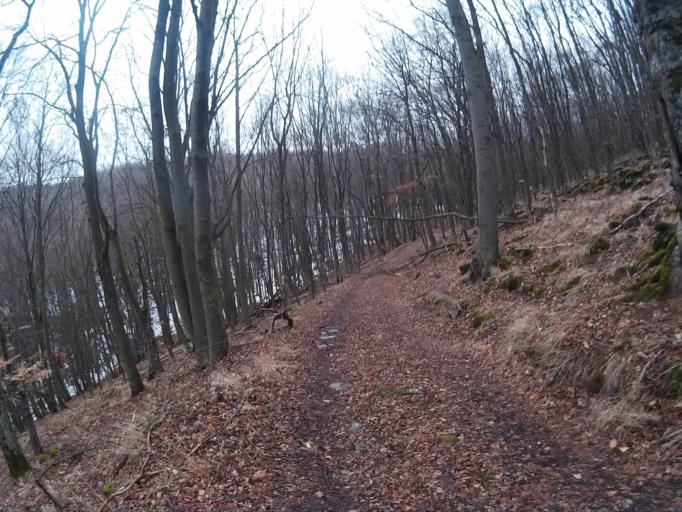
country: HU
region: Heves
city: Belapatfalva
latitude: 48.0492
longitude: 20.4055
